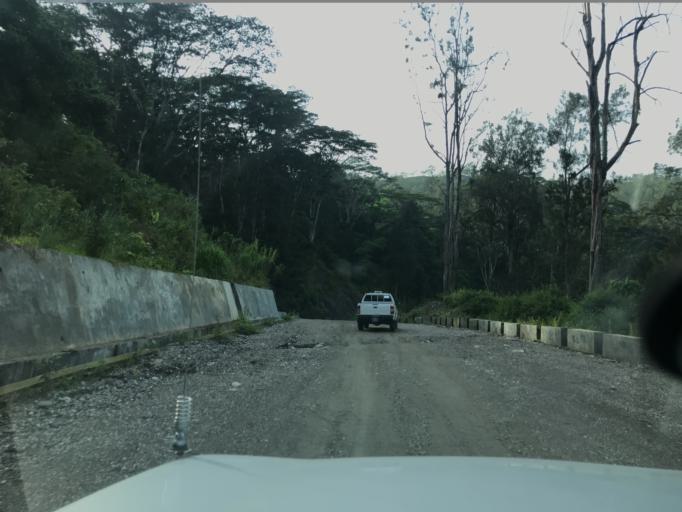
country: TL
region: Aileu
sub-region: Aileu Villa
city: Aileu
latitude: -8.6683
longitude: 125.5537
